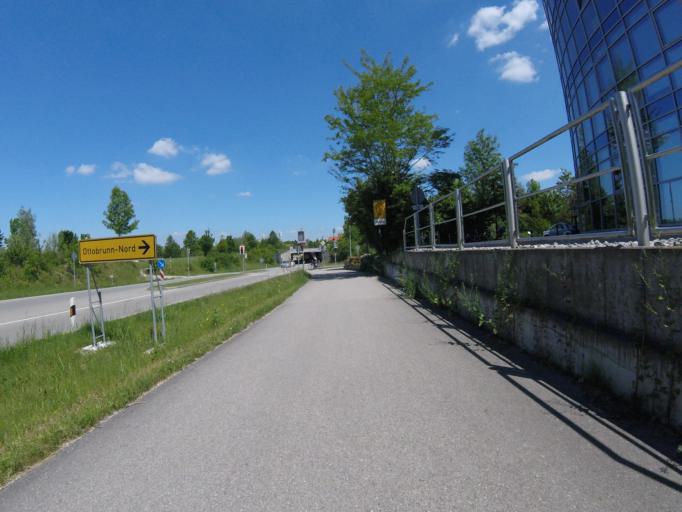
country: DE
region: Bavaria
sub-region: Upper Bavaria
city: Neubiberg
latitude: 48.0748
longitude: 11.6520
